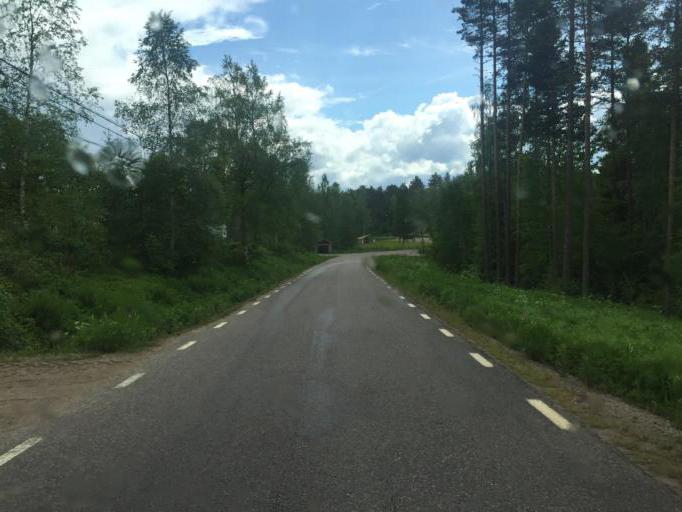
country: SE
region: Vaermland
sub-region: Hagfors Kommun
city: Hagfors
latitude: 60.2935
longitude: 13.8686
